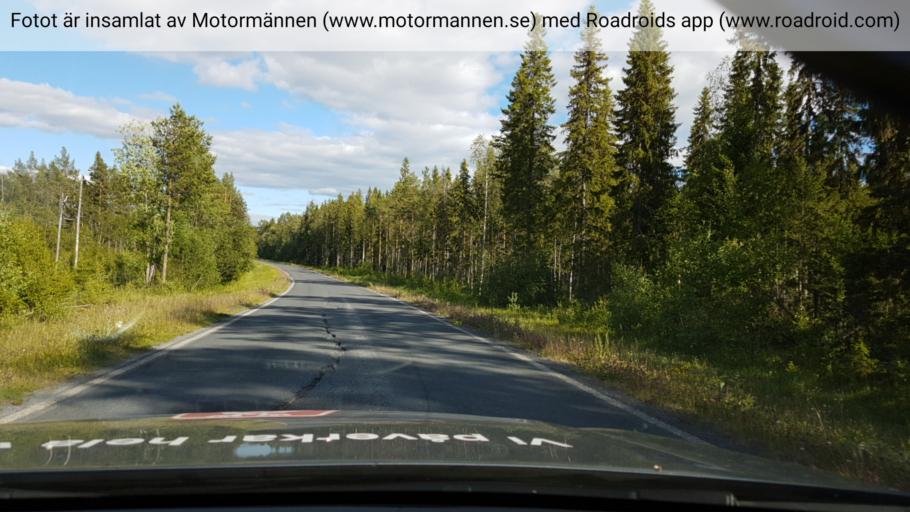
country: SE
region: Jaemtland
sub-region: Krokoms Kommun
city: Valla
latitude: 63.2874
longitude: 13.8760
